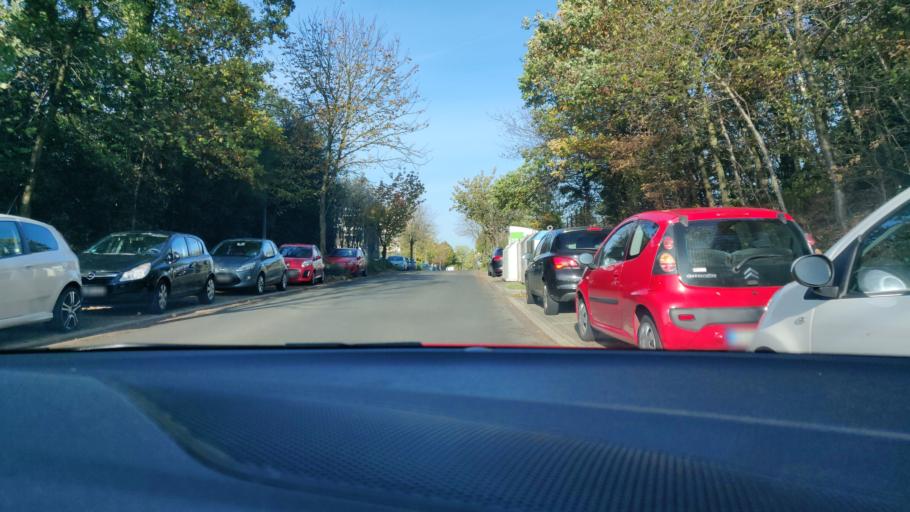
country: DE
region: North Rhine-Westphalia
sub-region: Regierungsbezirk Dusseldorf
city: Velbert
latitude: 51.3477
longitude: 7.0103
